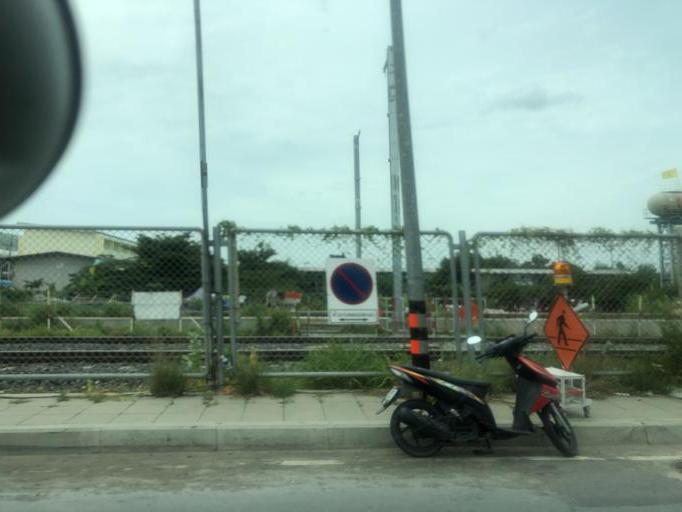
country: TH
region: Bangkok
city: Don Mueang
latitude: 13.9550
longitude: 100.6064
